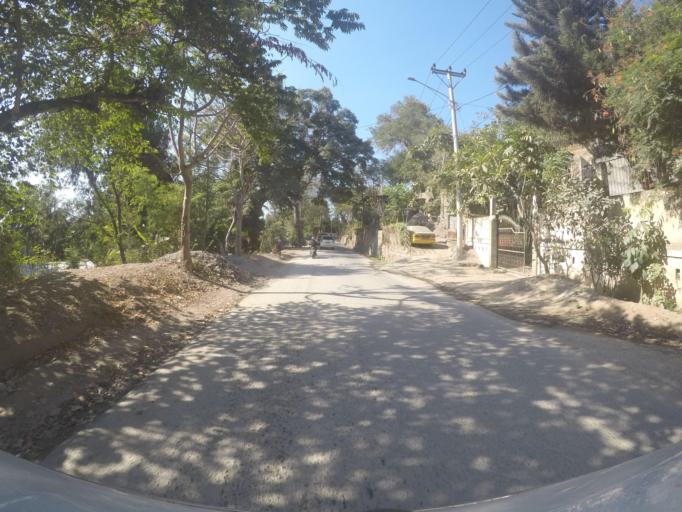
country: TL
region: Dili
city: Dili
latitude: -8.5677
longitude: 125.5482
